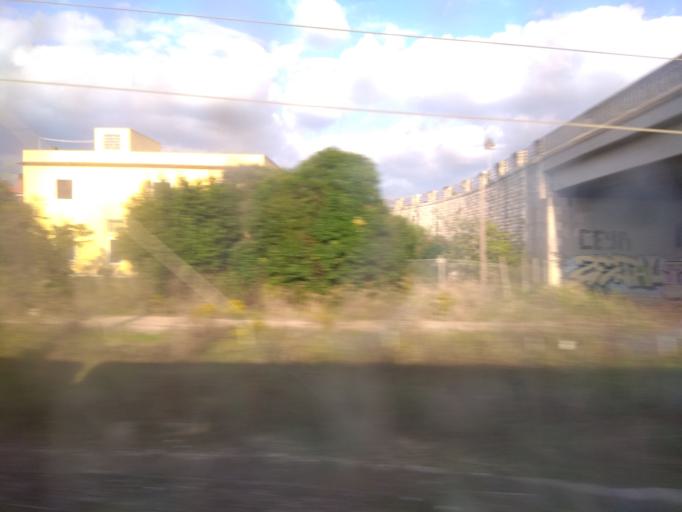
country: IT
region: Latium
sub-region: Citta metropolitana di Roma Capitale
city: Maccarese
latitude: 41.8731
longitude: 12.2432
